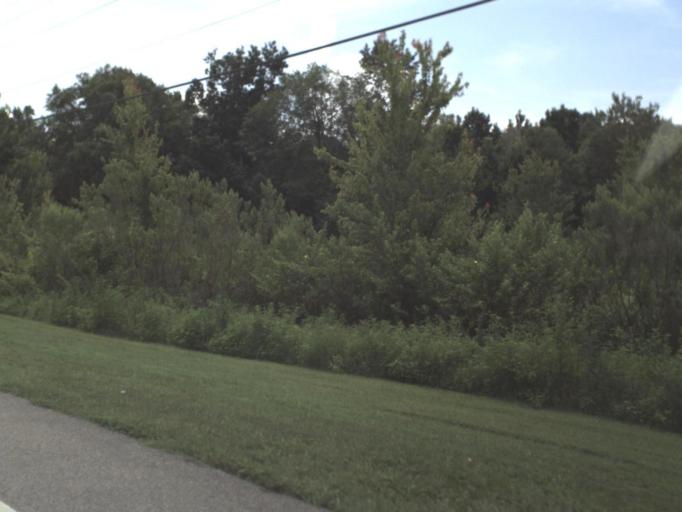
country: US
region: Florida
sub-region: Pasco County
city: Saint Leo
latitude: 28.3356
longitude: -82.2512
